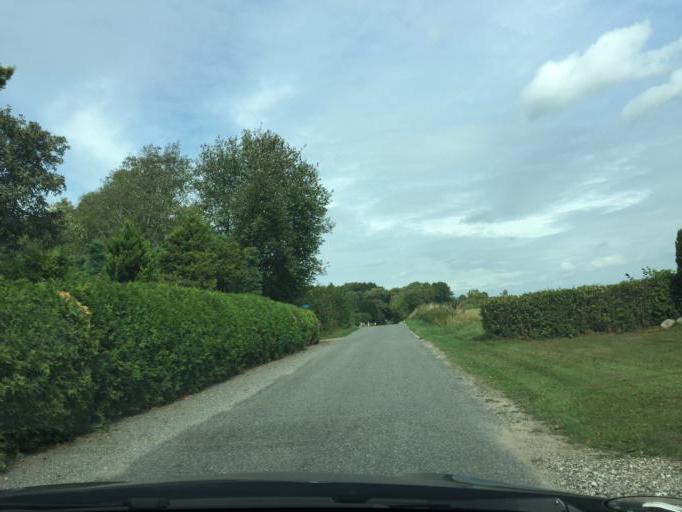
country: DK
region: South Denmark
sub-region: Assens Kommune
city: Vissenbjerg
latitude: 55.3585
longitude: 10.1422
